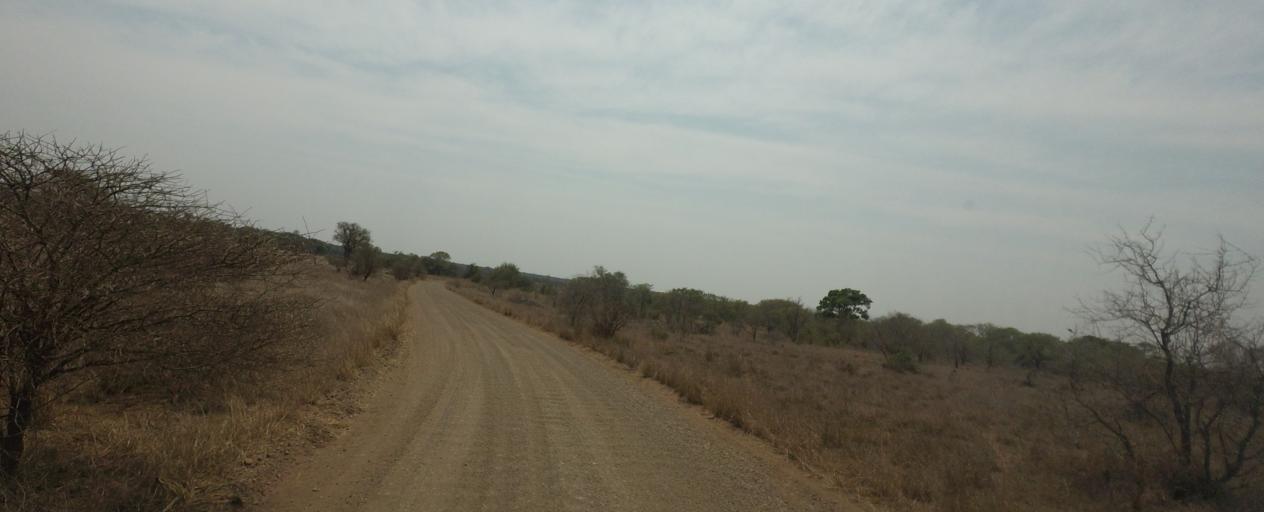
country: ZA
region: Limpopo
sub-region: Mopani District Municipality
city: Phalaborwa
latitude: -24.2622
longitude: 31.6499
